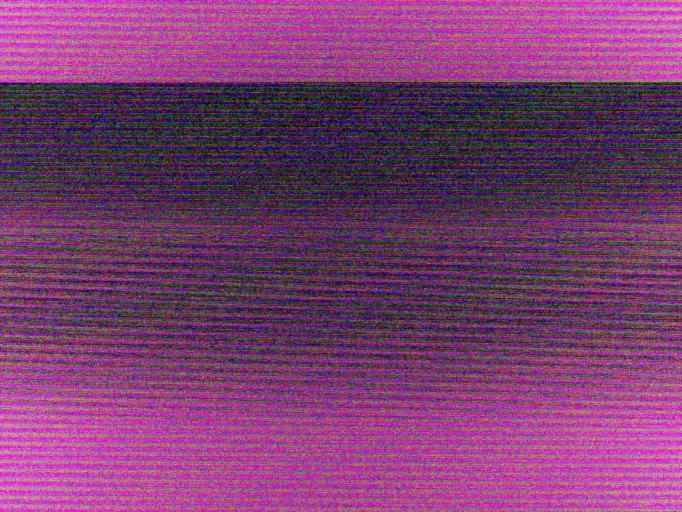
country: US
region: Massachusetts
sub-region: Middlesex County
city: Somerville
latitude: 42.3922
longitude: -71.1066
